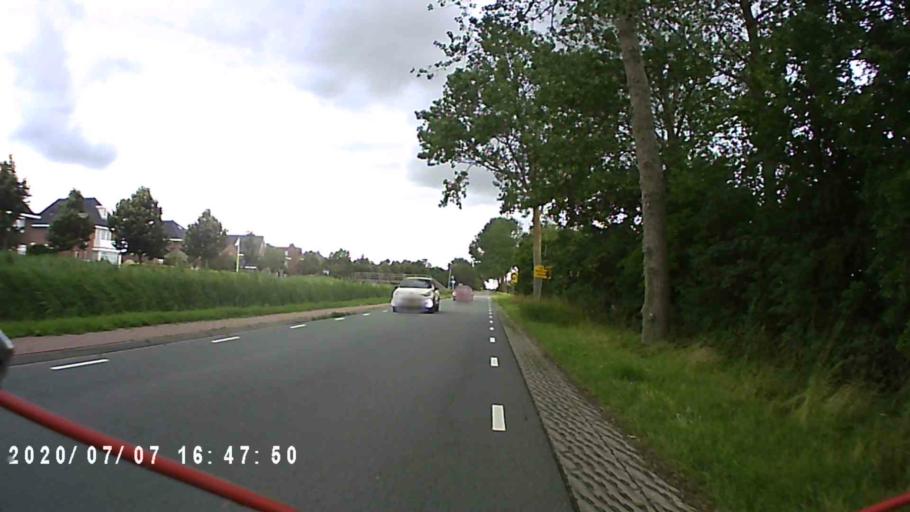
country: NL
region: Groningen
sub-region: Gemeente Winsum
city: Winsum
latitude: 53.3390
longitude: 6.5280
